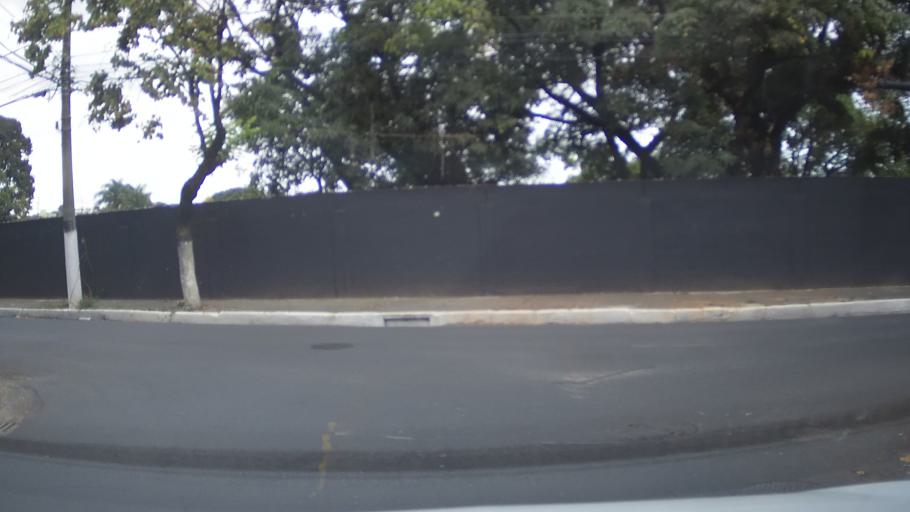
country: BR
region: Minas Gerais
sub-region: Belo Horizonte
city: Belo Horizonte
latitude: -19.8548
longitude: -43.9530
